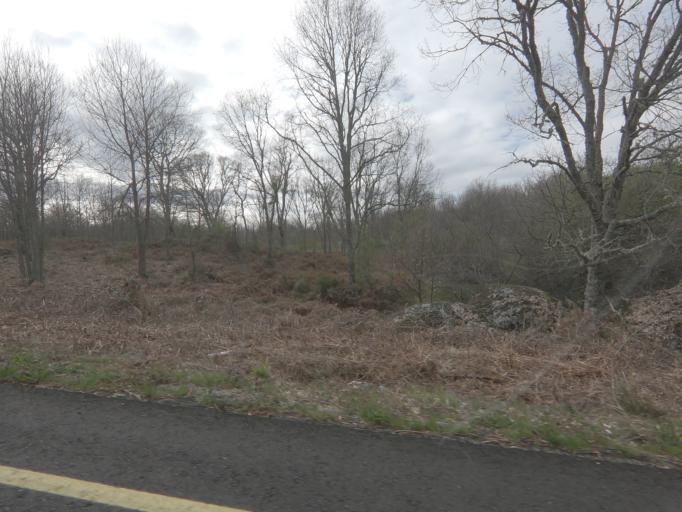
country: ES
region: Castille and Leon
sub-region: Provincia de Salamanca
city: Penaparda
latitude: 40.2680
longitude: -6.6880
